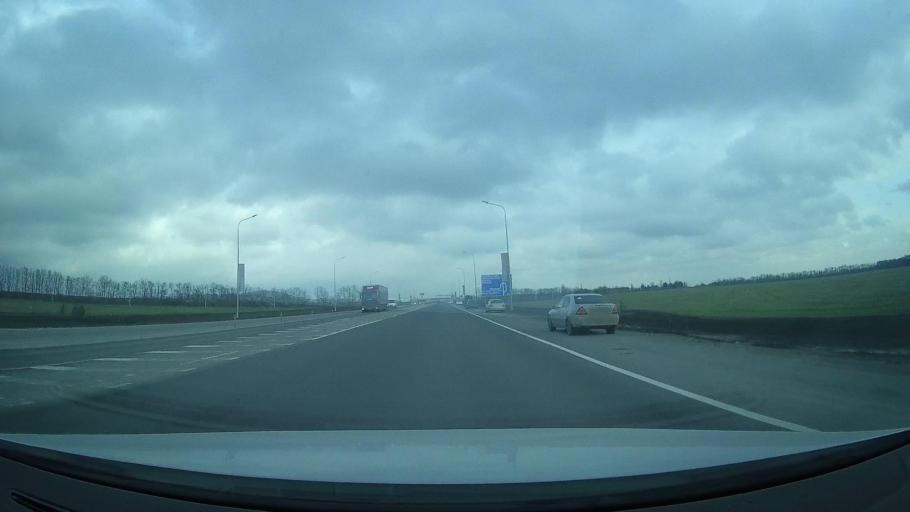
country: RU
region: Rostov
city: Grushevskaya
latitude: 47.4777
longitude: 39.9181
